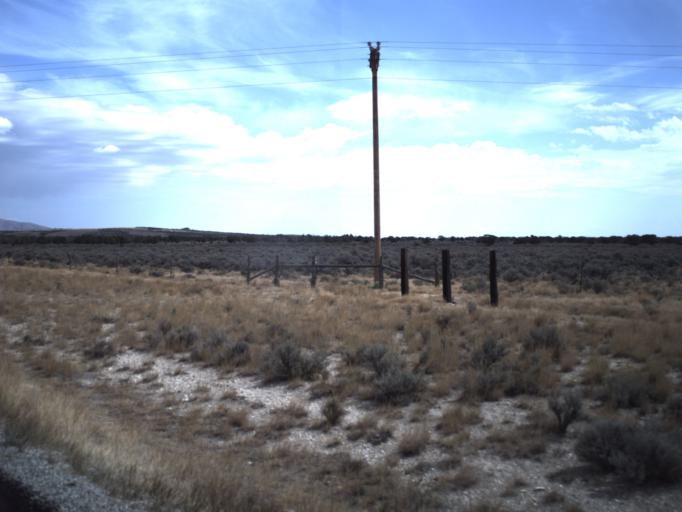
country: US
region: Idaho
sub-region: Cassia County
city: Burley
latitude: 41.7973
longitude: -113.4623
